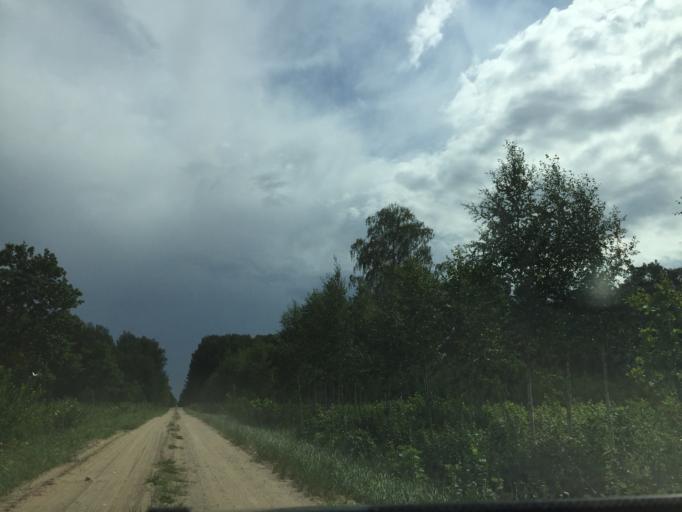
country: LT
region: Siauliu apskritis
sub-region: Joniskis
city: Joniskis
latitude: 56.3017
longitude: 23.6533
